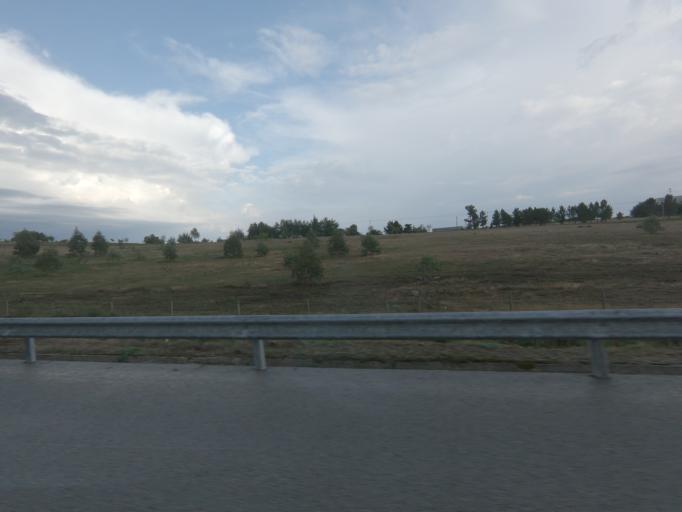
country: PT
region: Viseu
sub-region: Castro Daire
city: Castro Daire
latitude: 40.9468
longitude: -7.9008
